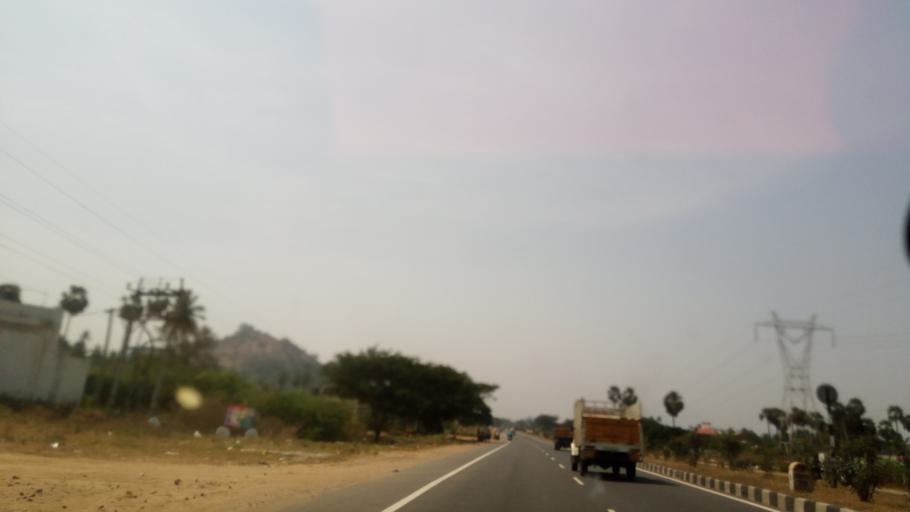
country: IN
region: Tamil Nadu
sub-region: Salem
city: Salem
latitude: 11.6516
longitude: 78.1925
